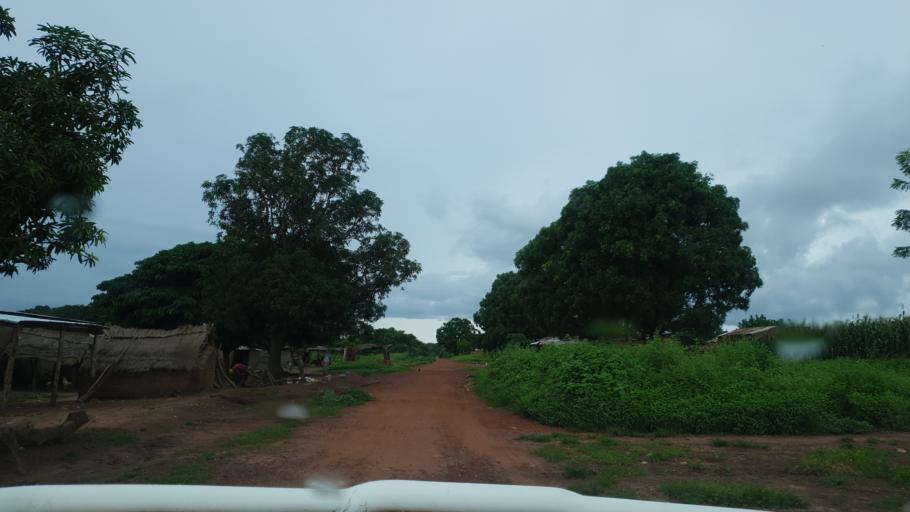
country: ML
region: Sikasso
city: Sikasso
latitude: 11.6742
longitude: -6.1681
